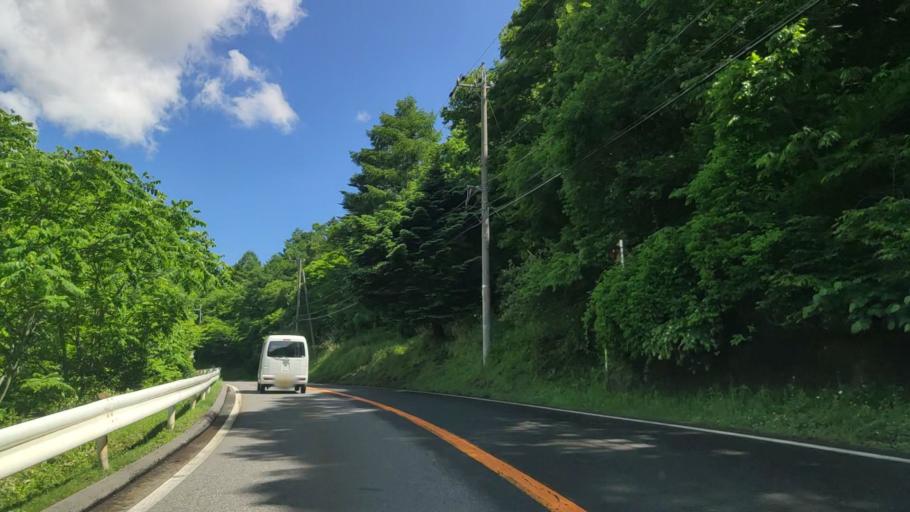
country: JP
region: Nagano
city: Chino
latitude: 36.0883
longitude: 138.2233
